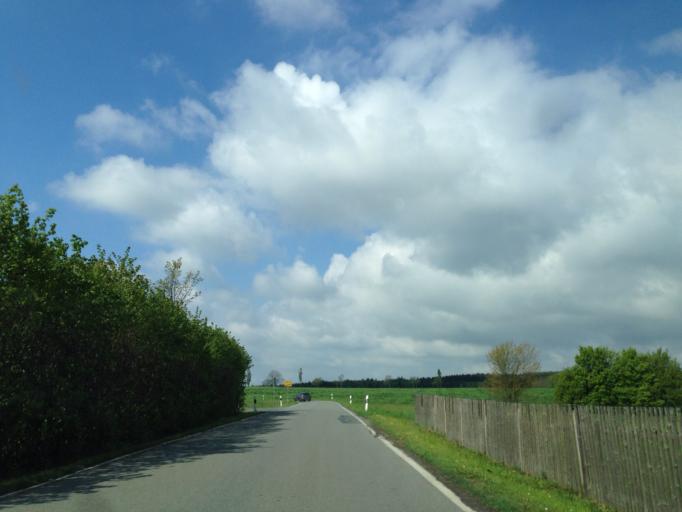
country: DE
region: Thuringia
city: Peuschen
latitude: 50.6587
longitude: 11.6395
